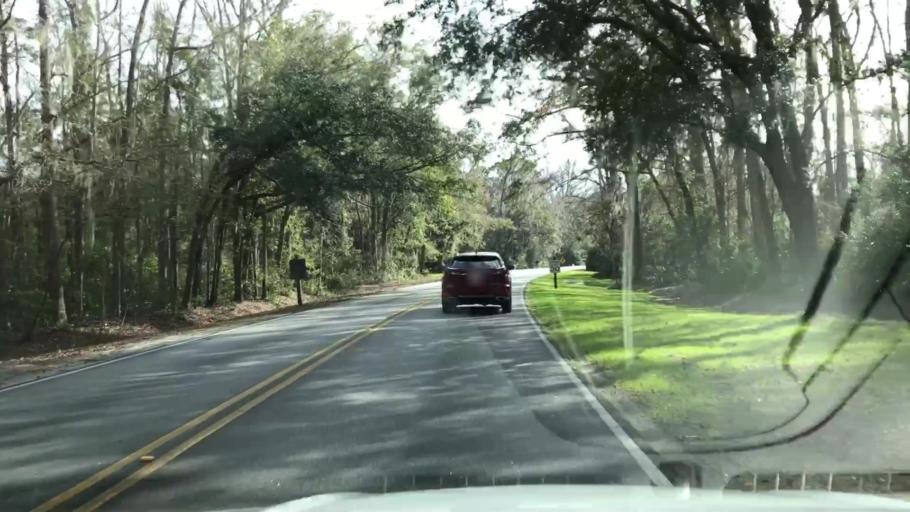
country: US
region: South Carolina
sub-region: Beaufort County
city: Hilton Head Island
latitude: 32.2241
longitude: -80.7231
